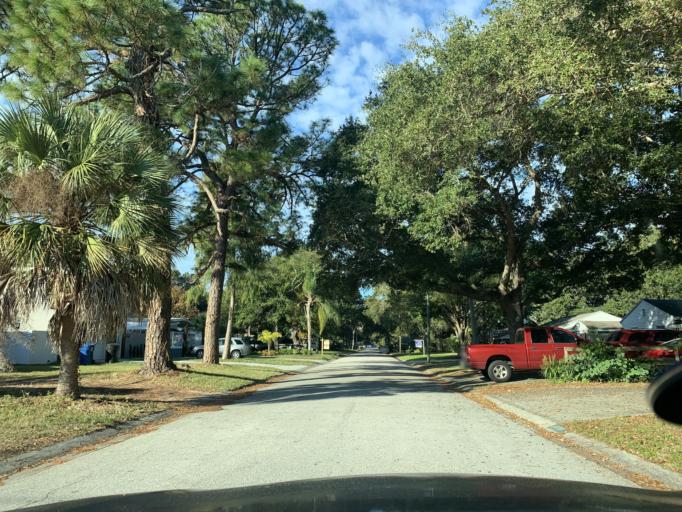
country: US
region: Florida
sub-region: Pinellas County
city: Bay Pines
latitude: 27.8045
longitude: -82.7499
